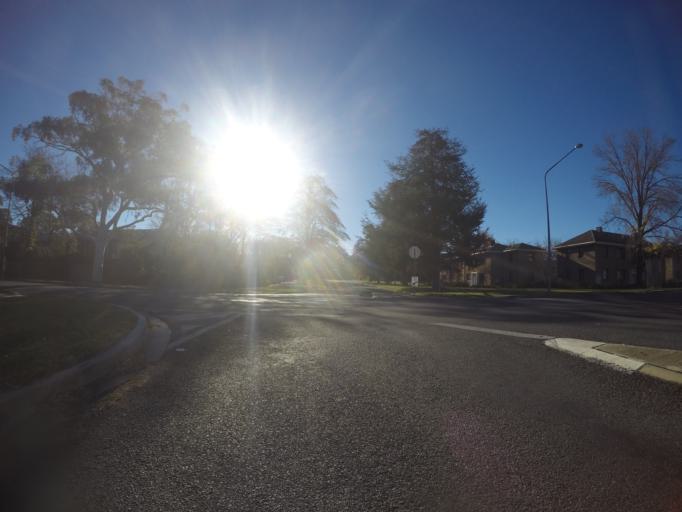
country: AU
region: Australian Capital Territory
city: Canberra
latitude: -35.2775
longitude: 149.1401
